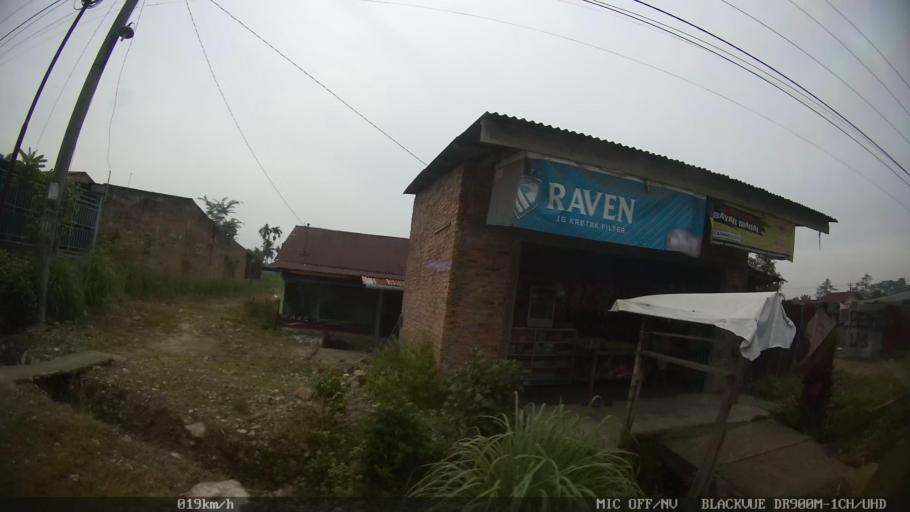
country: ID
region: North Sumatra
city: Deli Tua
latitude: 3.5417
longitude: 98.7349
